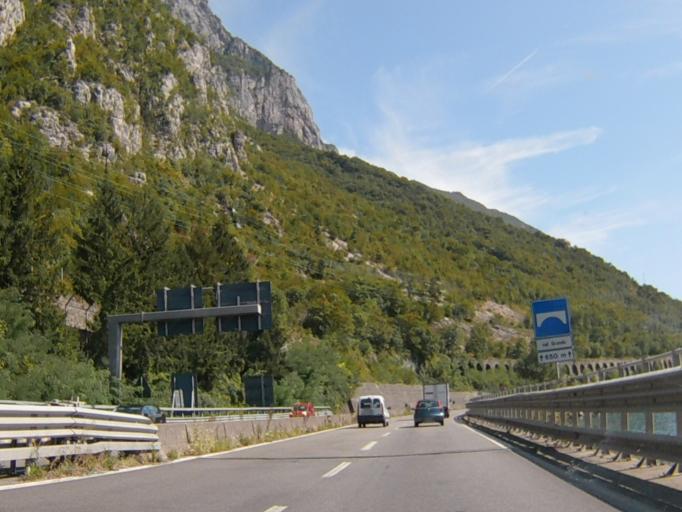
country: IT
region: Lombardy
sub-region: Provincia di Lecco
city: Abbadia Lariana
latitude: 45.8910
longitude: 9.3564
